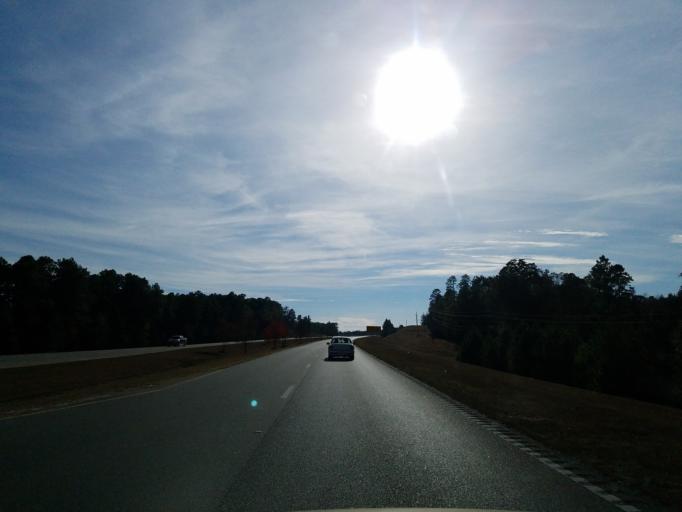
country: US
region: Mississippi
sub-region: Lamar County
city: West Hattiesburg
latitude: 31.2721
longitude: -89.3305
